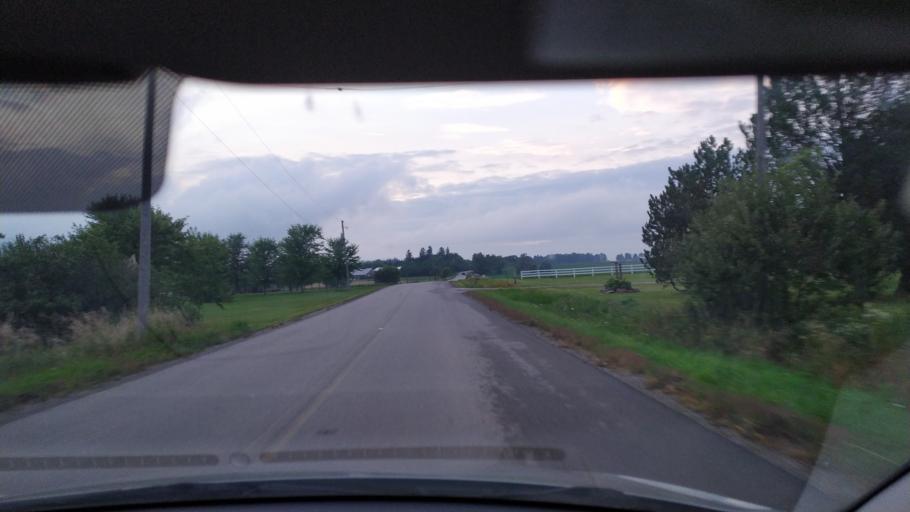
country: CA
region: Ontario
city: Kitchener
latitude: 43.3409
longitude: -80.6324
